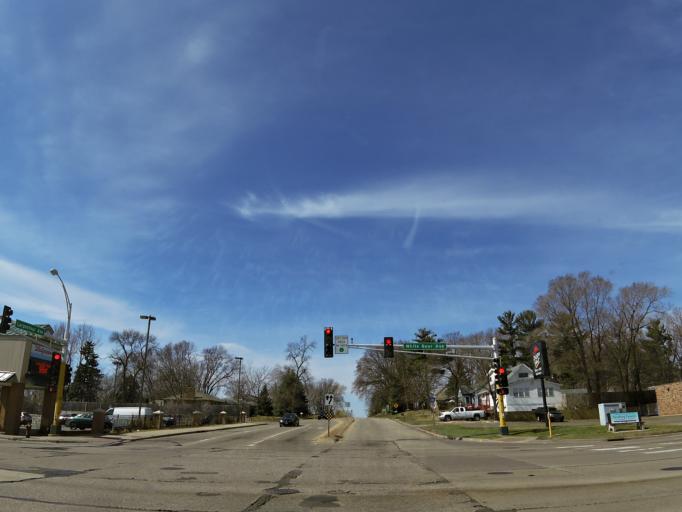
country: US
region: Minnesota
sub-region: Ramsey County
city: North Saint Paul
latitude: 44.9921
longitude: -93.0250
